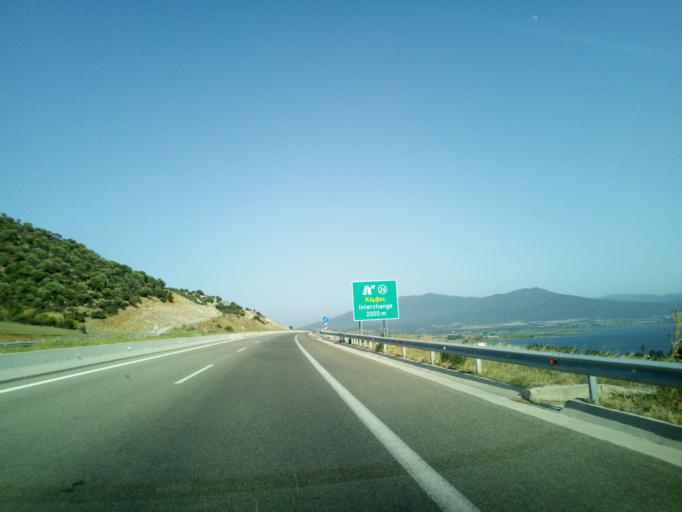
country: GR
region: Central Macedonia
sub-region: Nomos Thessalonikis
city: Nea Apollonia
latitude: 40.6826
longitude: 23.5601
